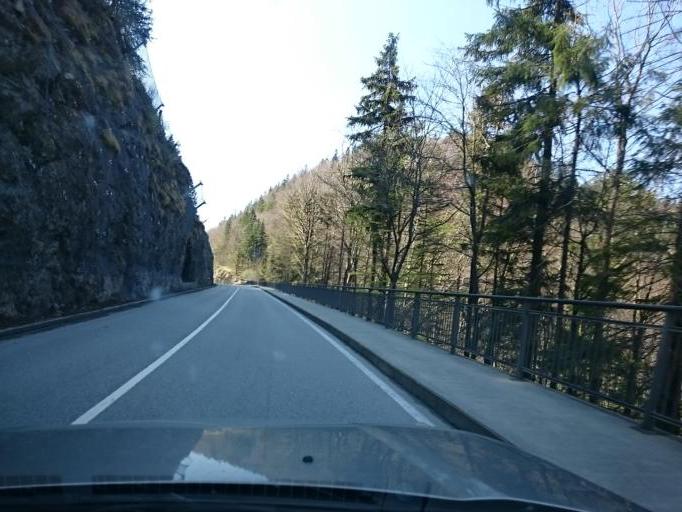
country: DE
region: Bavaria
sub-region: Upper Bavaria
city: Kochel
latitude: 47.6233
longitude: 11.3506
